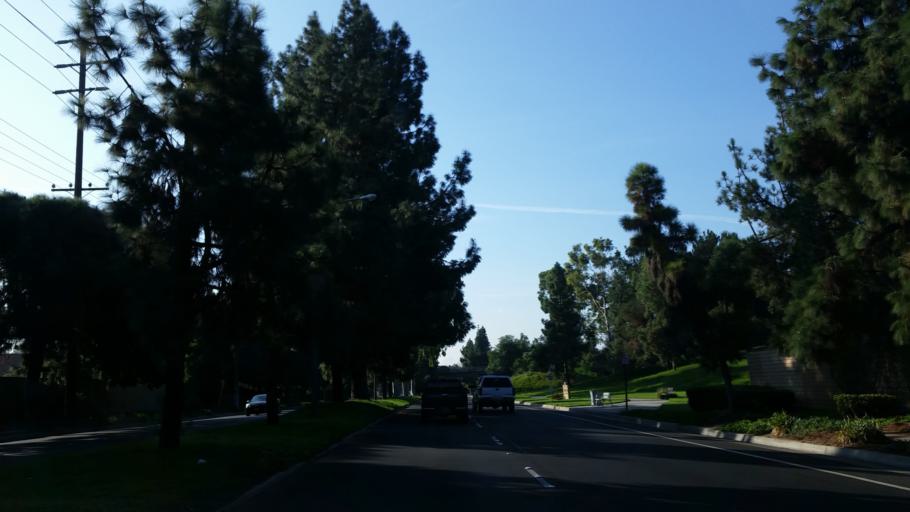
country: US
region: California
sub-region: Los Angeles County
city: Bellflower
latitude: 33.8797
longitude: -118.0999
